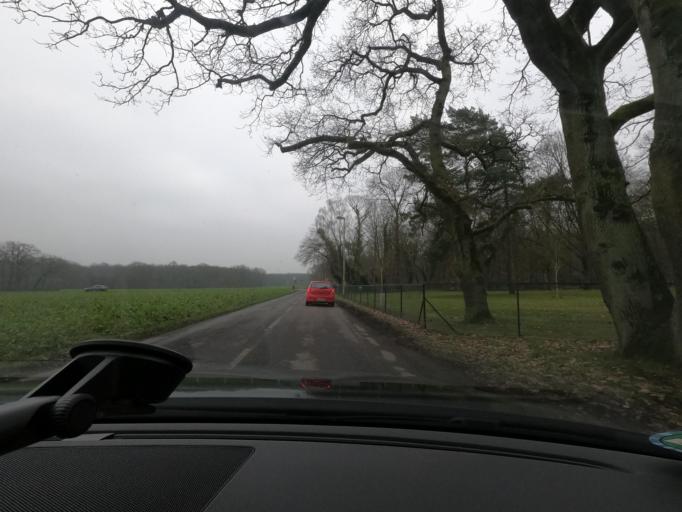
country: DE
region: North Rhine-Westphalia
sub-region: Regierungsbezirk Dusseldorf
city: Krefeld
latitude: 51.3935
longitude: 6.5385
